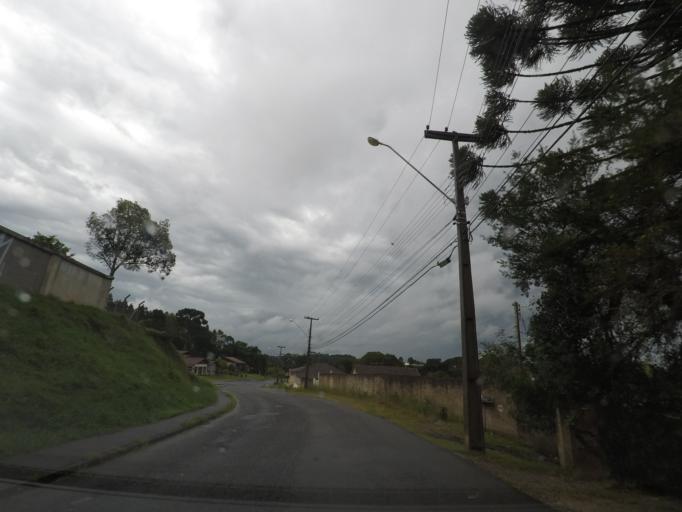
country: BR
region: Parana
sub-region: Campo Largo
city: Campo Largo
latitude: -25.4478
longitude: -49.4549
